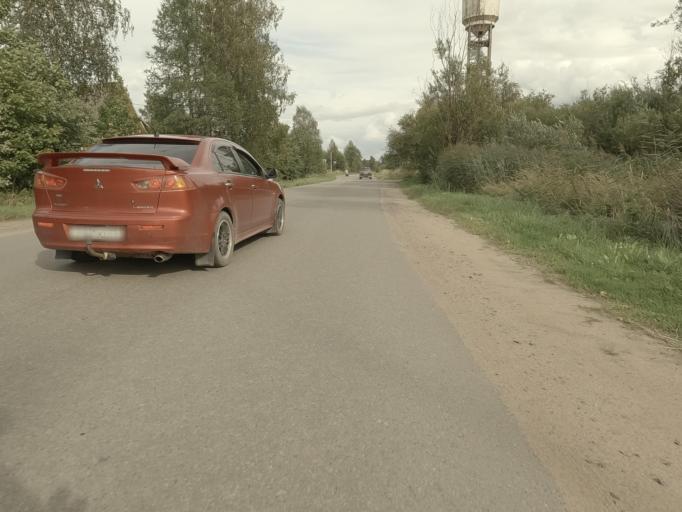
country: RU
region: Leningrad
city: Mga
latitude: 59.7553
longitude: 31.0742
